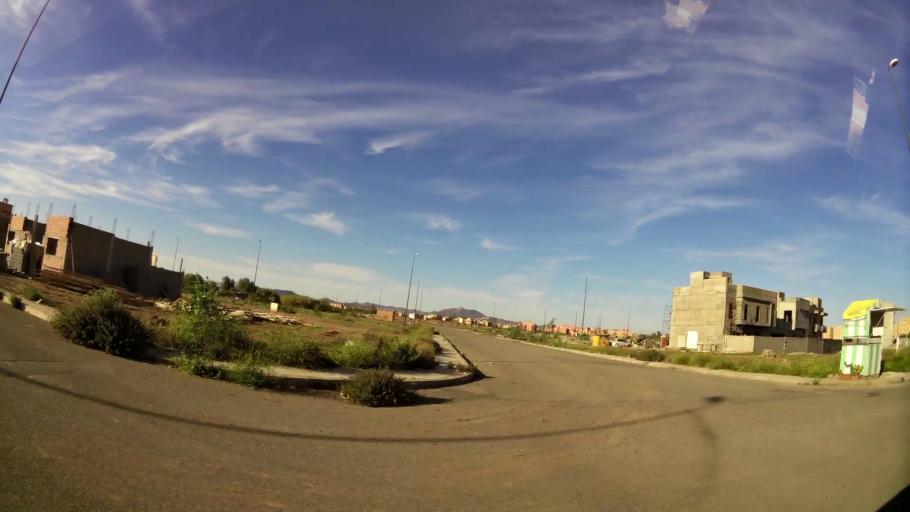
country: MA
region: Marrakech-Tensift-Al Haouz
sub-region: Marrakech
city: Marrakesh
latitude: 31.6721
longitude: -8.0706
